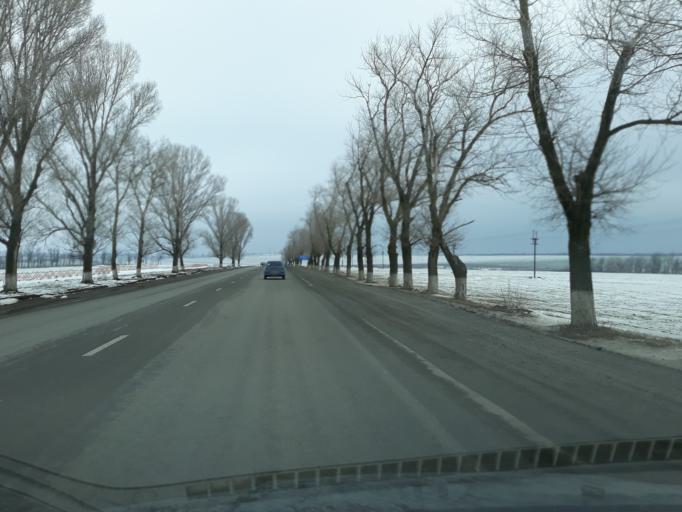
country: RU
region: Rostov
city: Primorka
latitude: 47.3155
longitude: 39.1007
